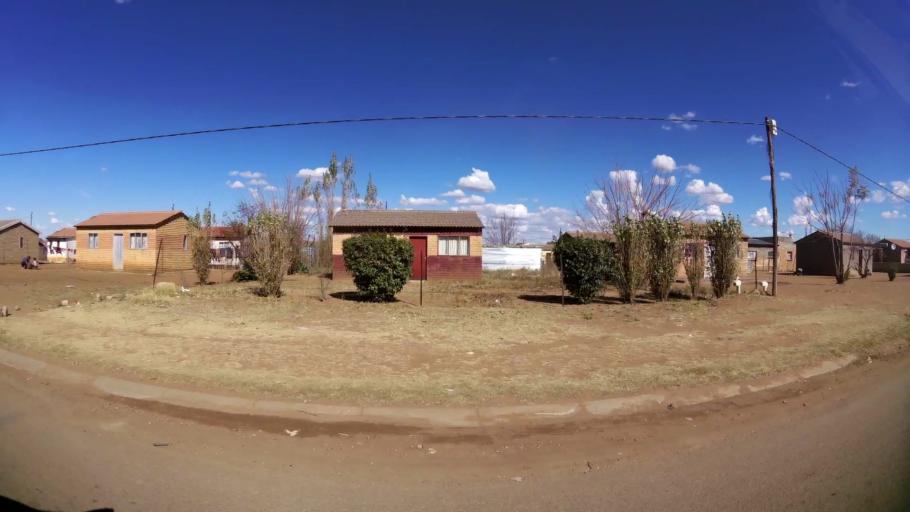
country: ZA
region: North-West
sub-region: Dr Kenneth Kaunda District Municipality
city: Klerksdorp
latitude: -26.8745
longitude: 26.5712
